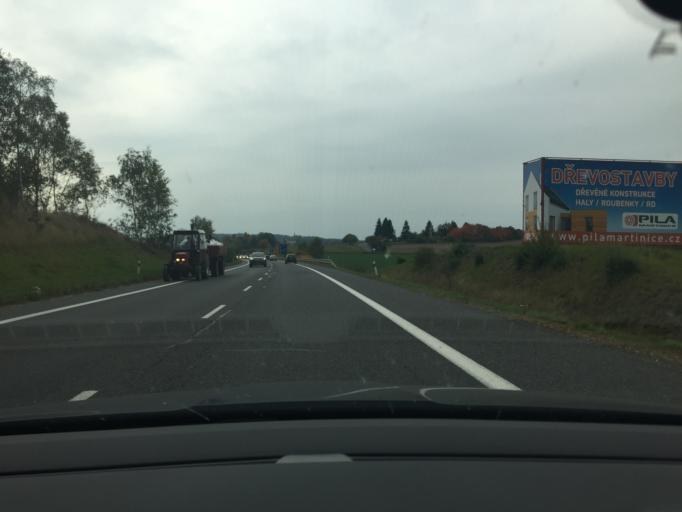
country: CZ
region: Central Bohemia
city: Milin
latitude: 49.6473
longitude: 14.0513
